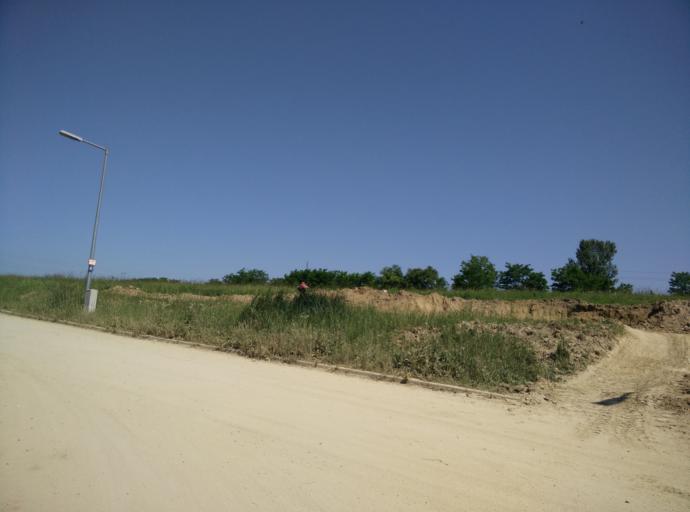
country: HU
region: Pest
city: Biatorbagy
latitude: 47.4715
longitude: 18.8443
